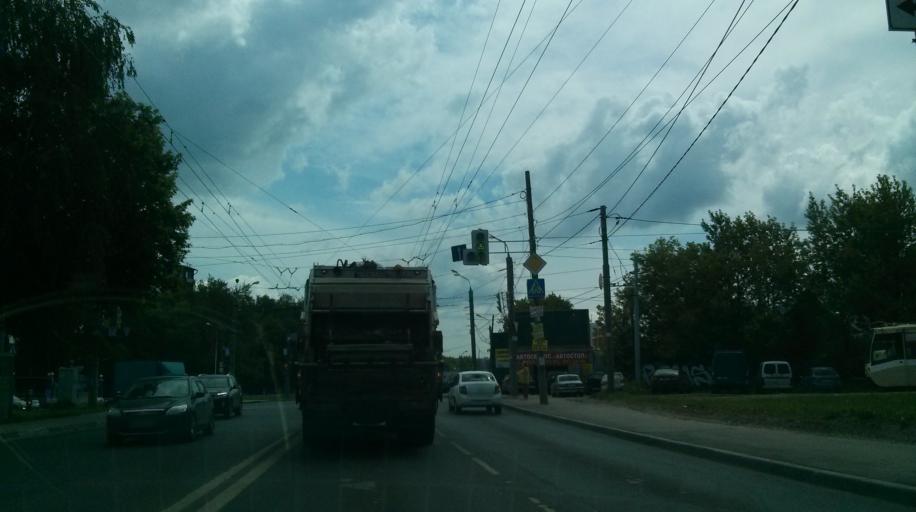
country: RU
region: Nizjnij Novgorod
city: Nizhniy Novgorod
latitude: 56.3007
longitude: 44.0313
